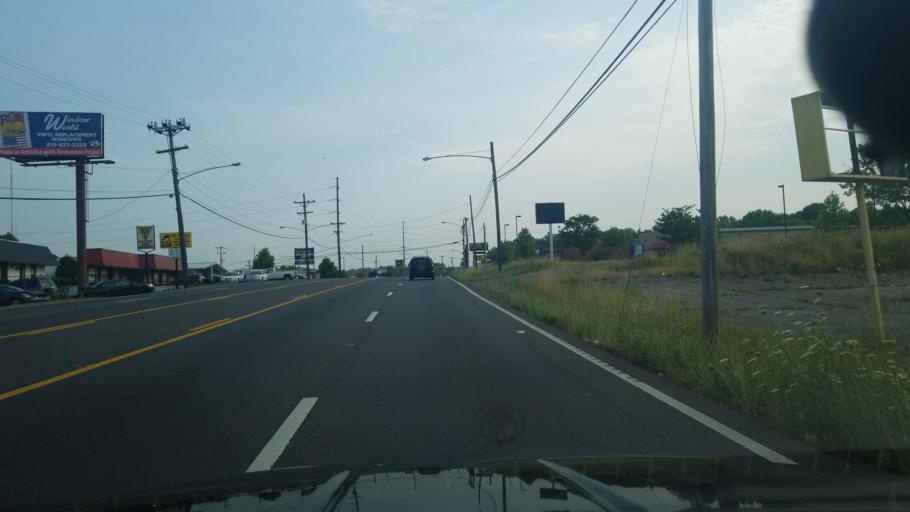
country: US
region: Tennessee
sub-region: Davidson County
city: Goodlettsville
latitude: 36.2670
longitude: -86.7565
